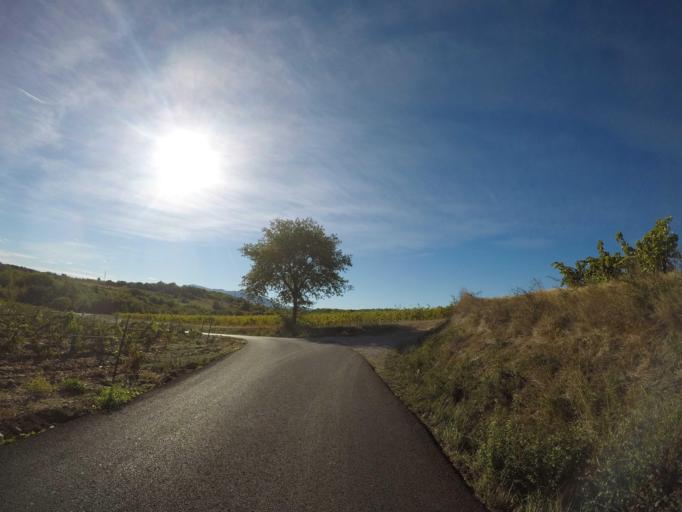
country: FR
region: Languedoc-Roussillon
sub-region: Departement des Pyrenees-Orientales
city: Trouillas
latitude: 42.5749
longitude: 2.7885
